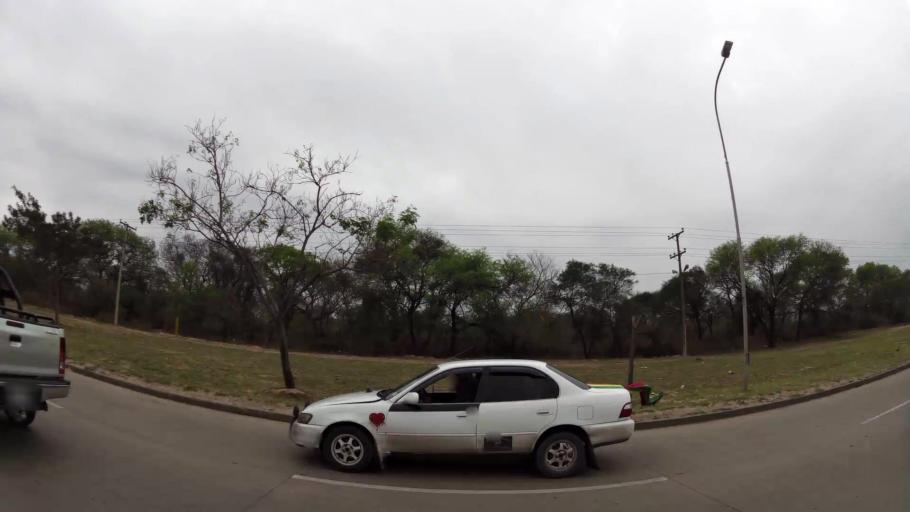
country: BO
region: Santa Cruz
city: Santa Cruz de la Sierra
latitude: -17.7624
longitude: -63.2032
